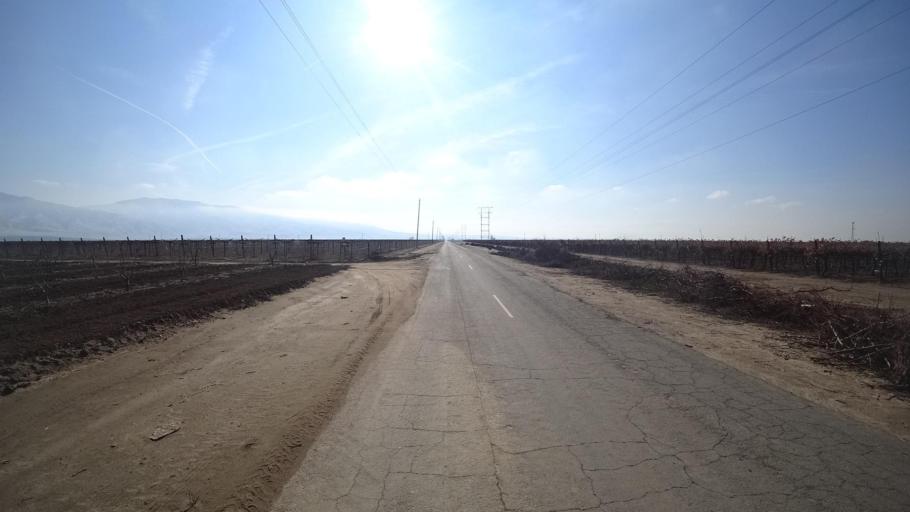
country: US
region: California
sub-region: Kern County
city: Arvin
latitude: 35.2577
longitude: -118.8070
